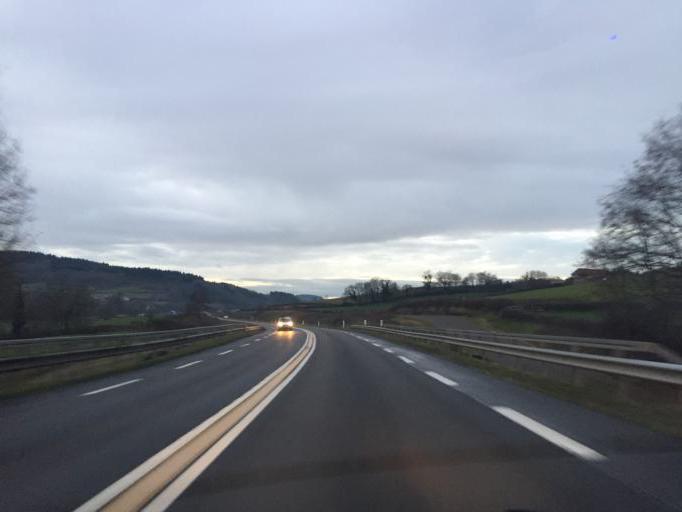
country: FR
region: Bourgogne
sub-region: Departement de Saone-et-Loire
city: Matour
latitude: 46.3713
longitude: 4.5510
